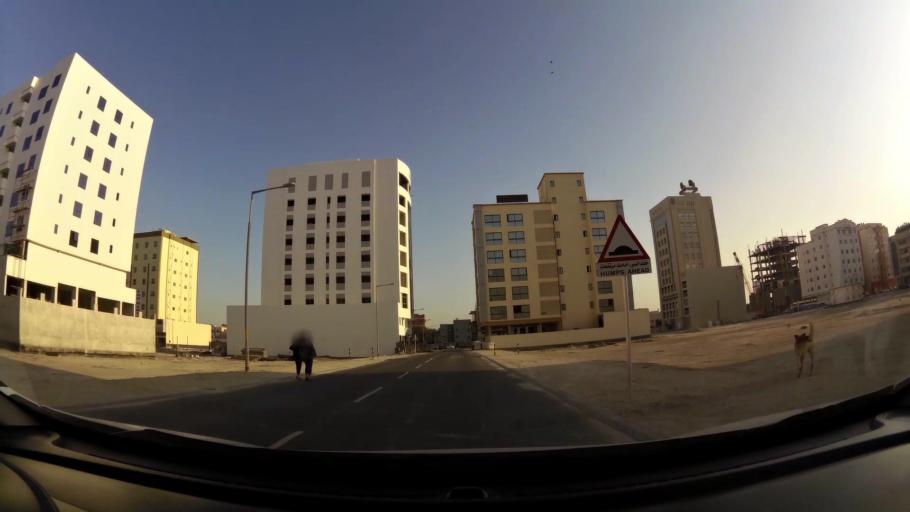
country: BH
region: Manama
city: Jidd Hafs
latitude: 26.2264
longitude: 50.5568
